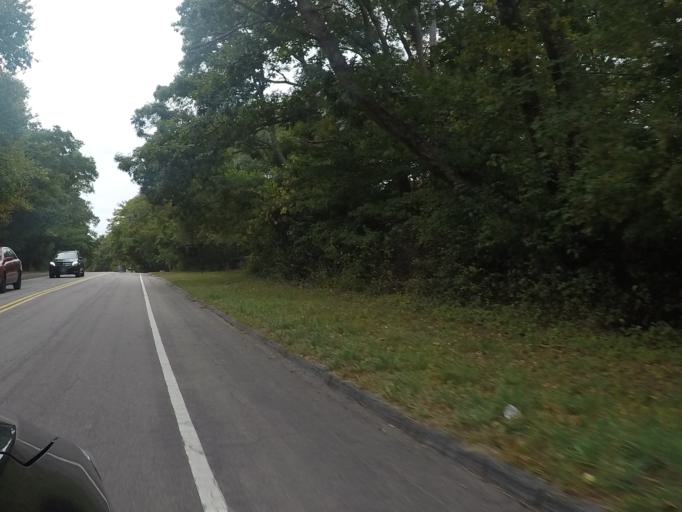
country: US
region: Massachusetts
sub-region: Bristol County
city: Smith Mills
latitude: 41.6346
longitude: -71.0009
